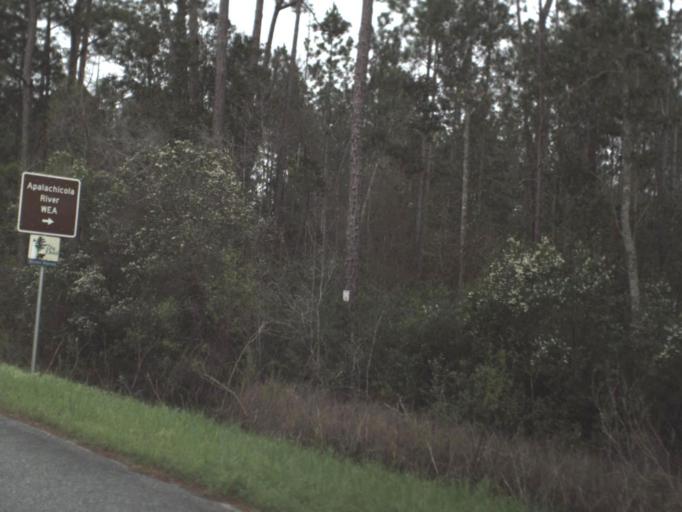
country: US
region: Florida
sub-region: Franklin County
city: Eastpoint
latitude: 29.8233
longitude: -84.9112
